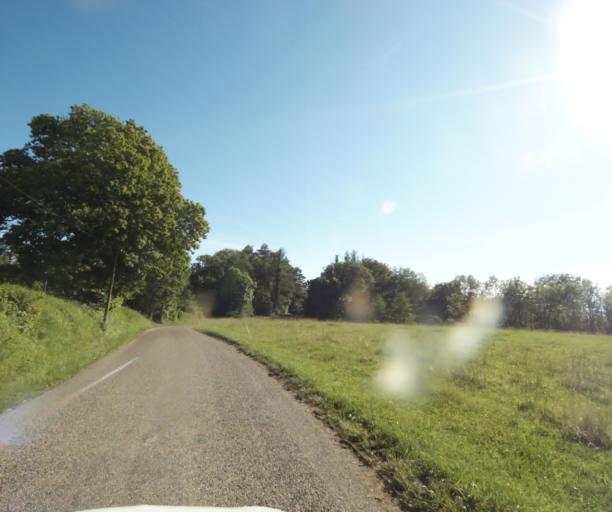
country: FR
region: Rhone-Alpes
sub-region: Departement de la Haute-Savoie
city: Ballaison
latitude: 46.3042
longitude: 6.3333
